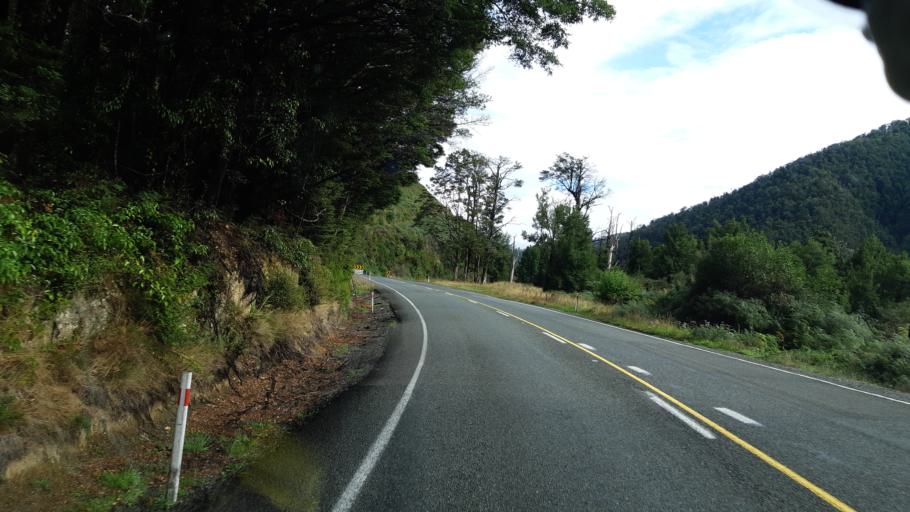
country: NZ
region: West Coast
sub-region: Buller District
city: Westport
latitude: -42.0080
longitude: 172.2349
